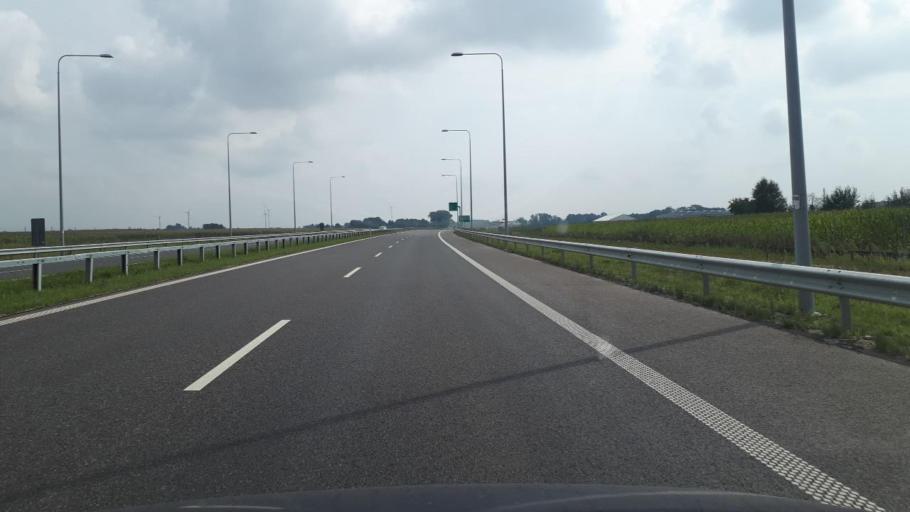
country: PL
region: Greater Poland Voivodeship
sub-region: Powiat kepinski
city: Kepno
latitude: 51.3076
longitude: 18.0161
